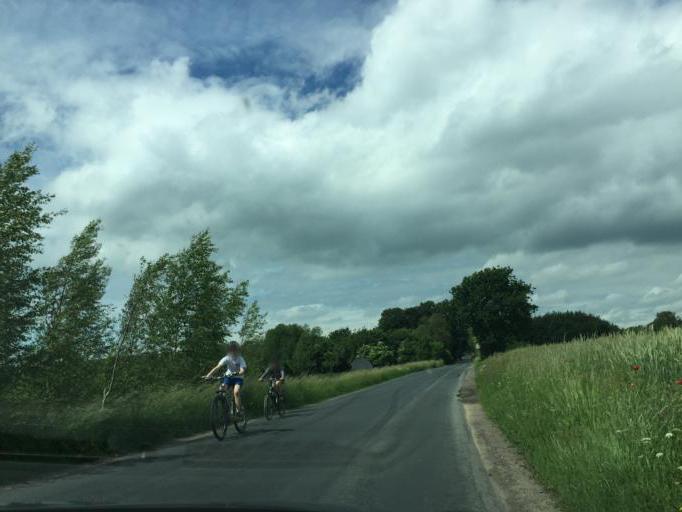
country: DK
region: South Denmark
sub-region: Faaborg-Midtfyn Kommune
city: Ringe
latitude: 55.2052
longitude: 10.4428
